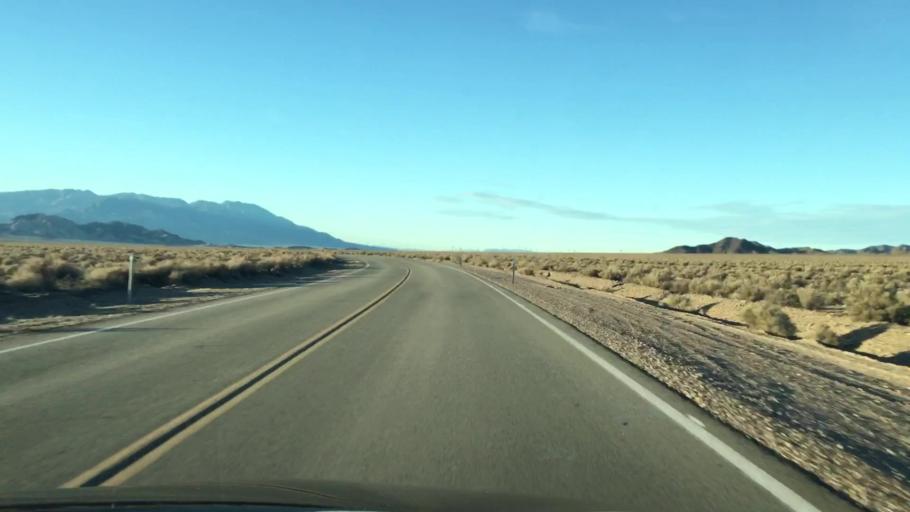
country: US
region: California
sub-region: San Bernardino County
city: Fort Irwin
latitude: 35.3456
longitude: -116.0847
